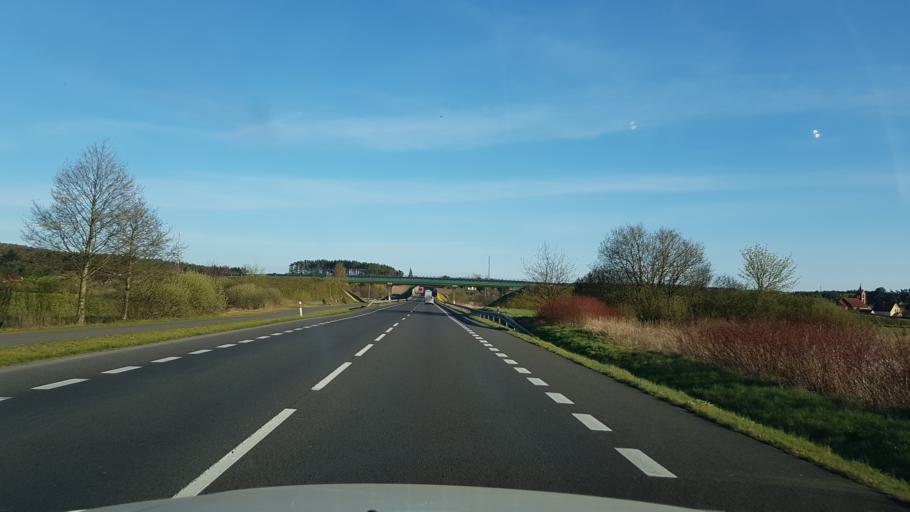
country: PL
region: West Pomeranian Voivodeship
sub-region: Powiat kamienski
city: Wolin
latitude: 53.8763
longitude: 14.5357
